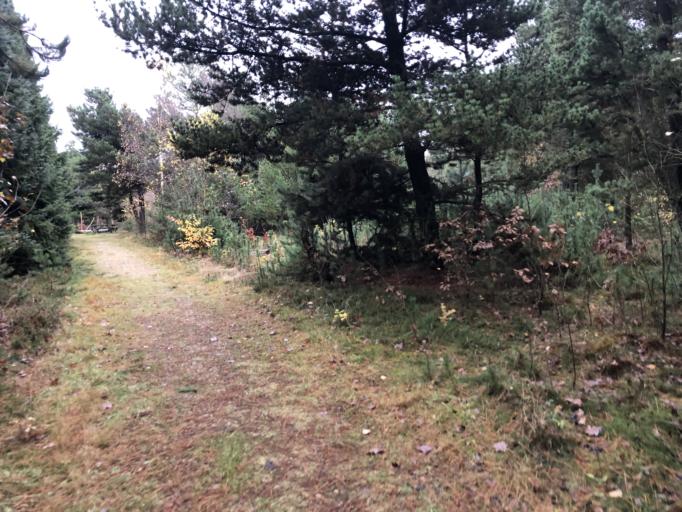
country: DK
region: Central Jutland
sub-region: Holstebro Kommune
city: Ulfborg
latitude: 56.3136
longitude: 8.2039
